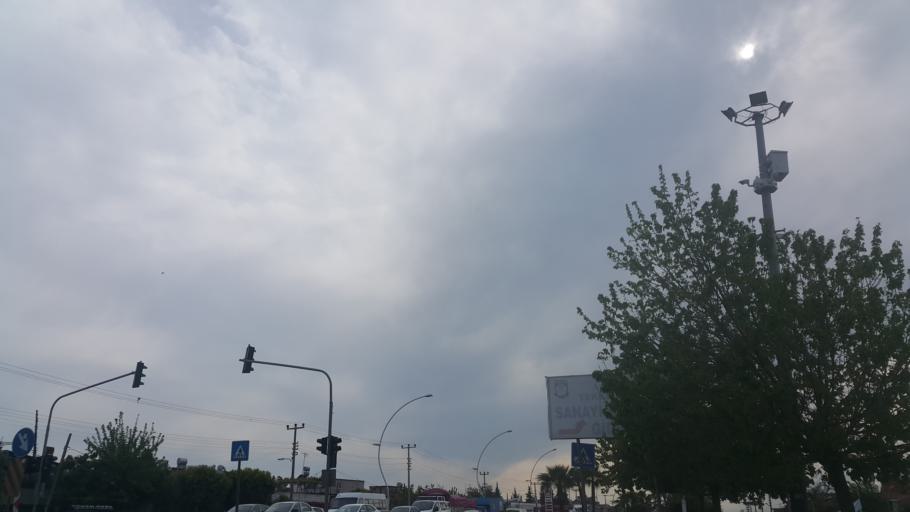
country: TR
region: Mersin
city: Tarsus
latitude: 36.9143
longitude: 34.9150
